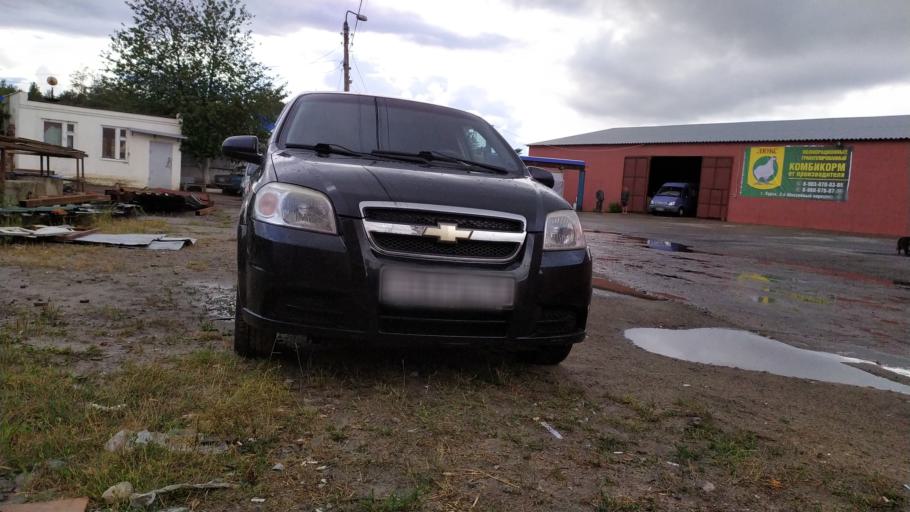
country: RU
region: Kursk
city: Kursk
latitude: 51.6997
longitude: 36.1748
